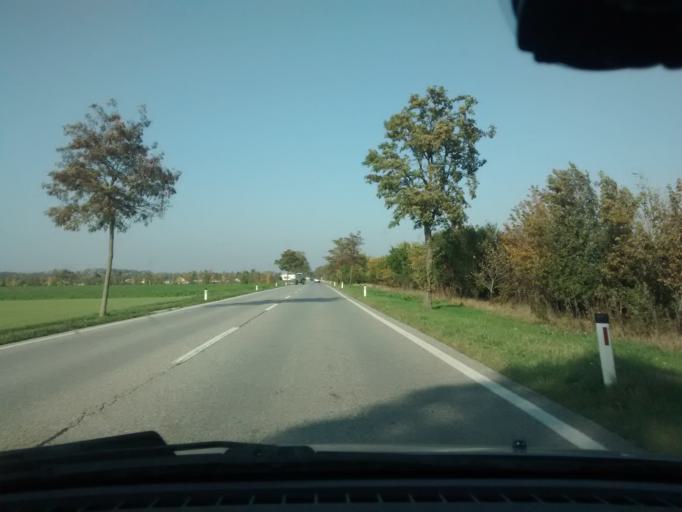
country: AT
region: Lower Austria
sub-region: Politischer Bezirk Modling
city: Munchendorf
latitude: 48.0523
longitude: 16.3822
